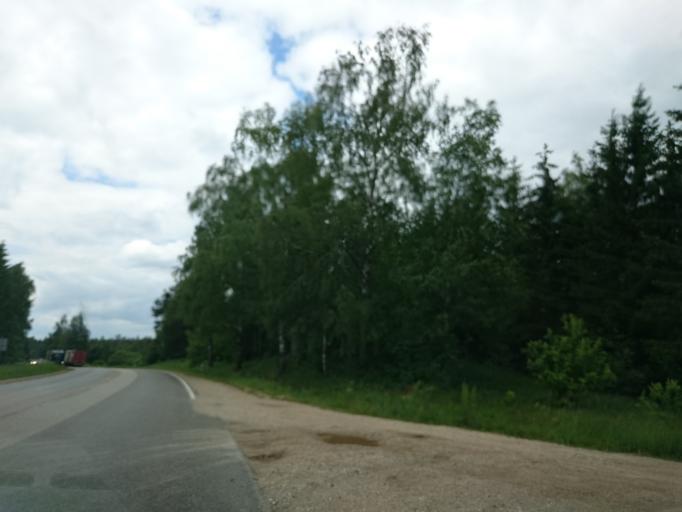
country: LV
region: Ludzas Rajons
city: Ludza
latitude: 56.5367
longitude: 27.5792
